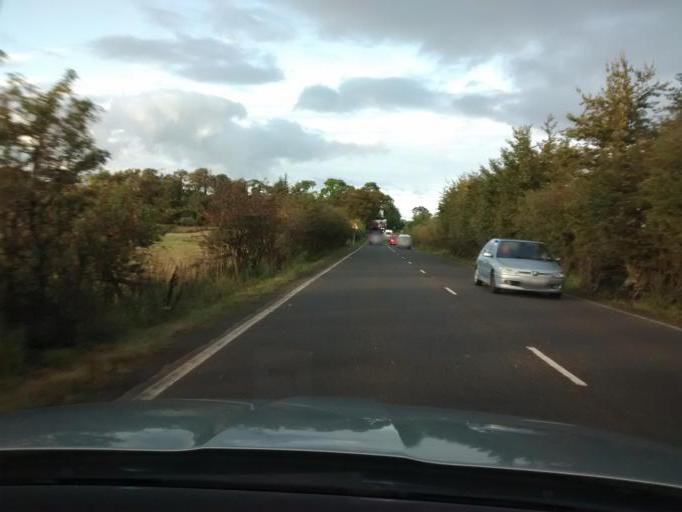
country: GB
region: Scotland
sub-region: Renfrewshire
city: Lochwinnoch
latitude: 55.7879
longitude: -4.6046
